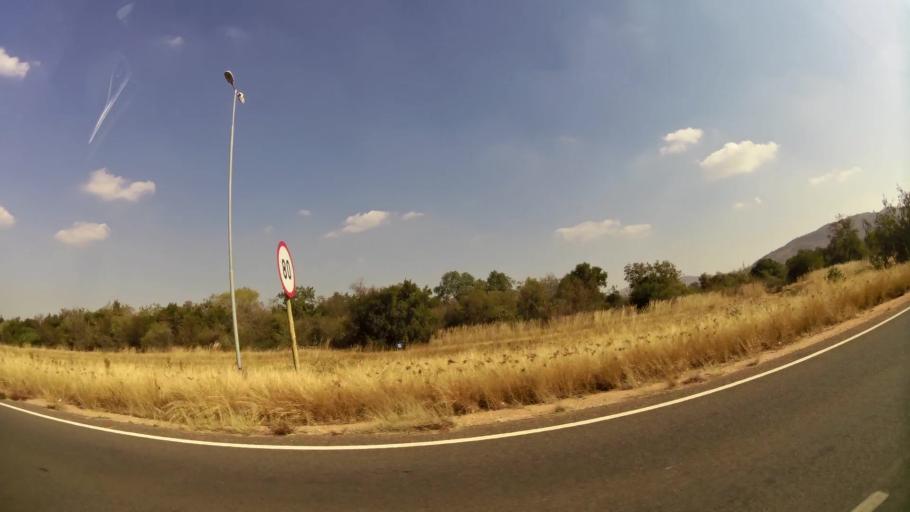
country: ZA
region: North-West
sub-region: Bojanala Platinum District Municipality
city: Rustenburg
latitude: -25.5507
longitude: 27.1335
